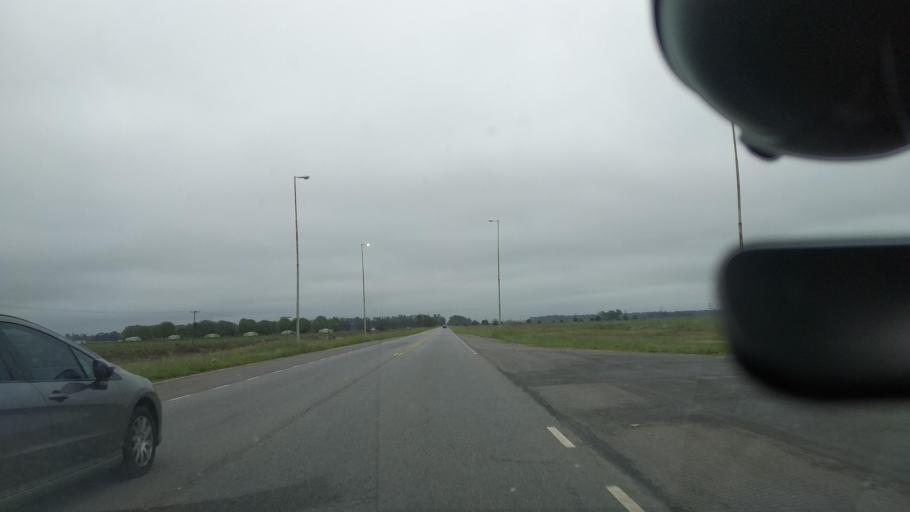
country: AR
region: Buenos Aires
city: Veronica
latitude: -35.3304
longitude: -57.4640
